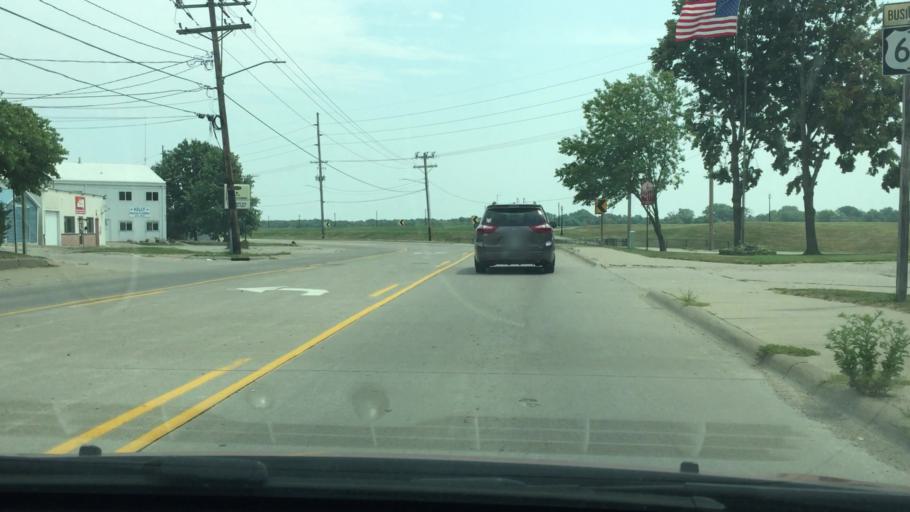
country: US
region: Iowa
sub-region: Muscatine County
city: Muscatine
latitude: 41.4153
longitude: -91.0553
